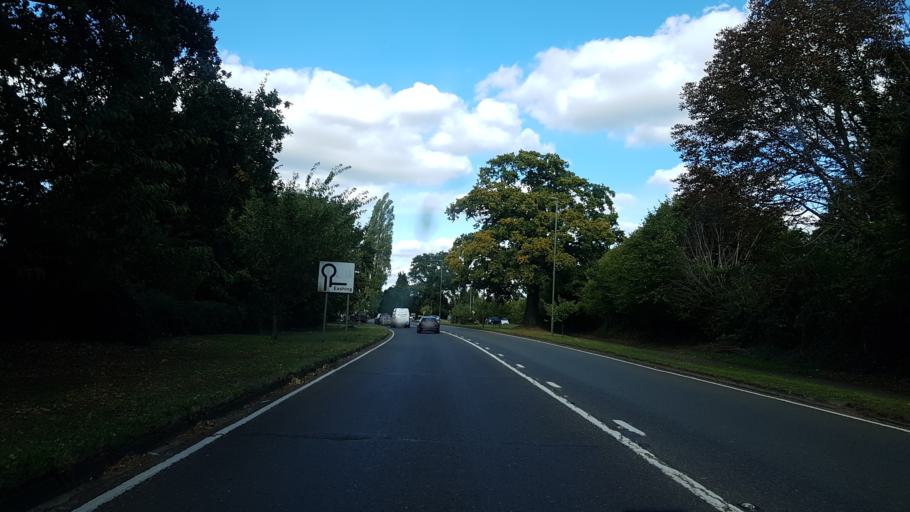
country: GB
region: England
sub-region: Surrey
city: Milford
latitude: 51.1746
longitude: -0.6495
